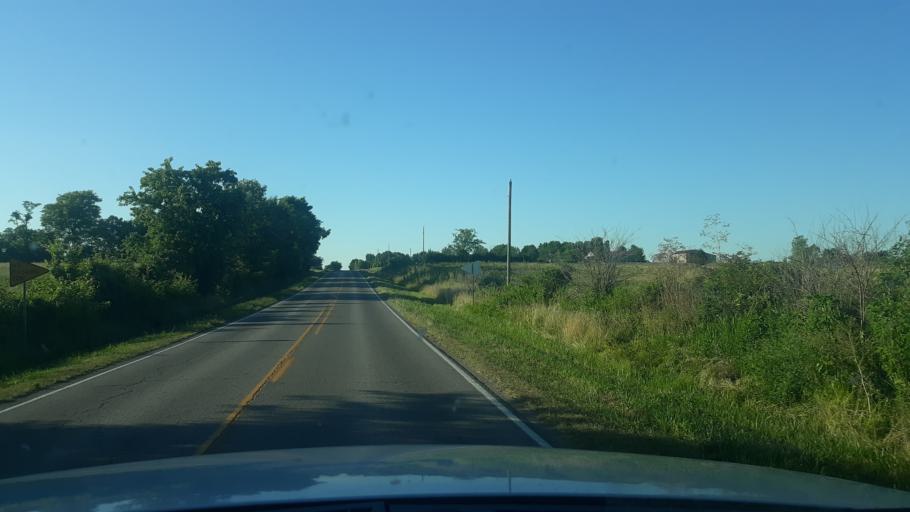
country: US
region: Illinois
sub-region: Saline County
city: Harrisburg
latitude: 37.8541
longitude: -88.6055
